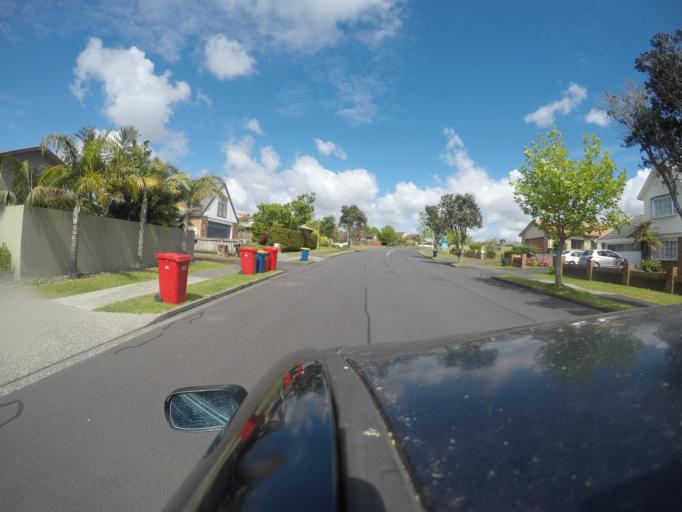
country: NZ
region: Auckland
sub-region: Auckland
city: Rosebank
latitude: -36.8179
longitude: 174.6376
